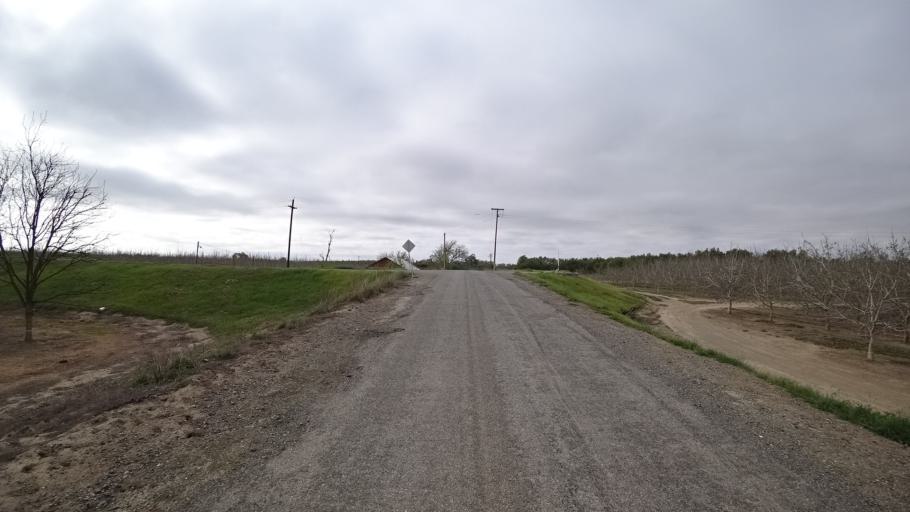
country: US
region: California
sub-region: Colusa County
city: Colusa
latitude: 39.4066
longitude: -122.0013
